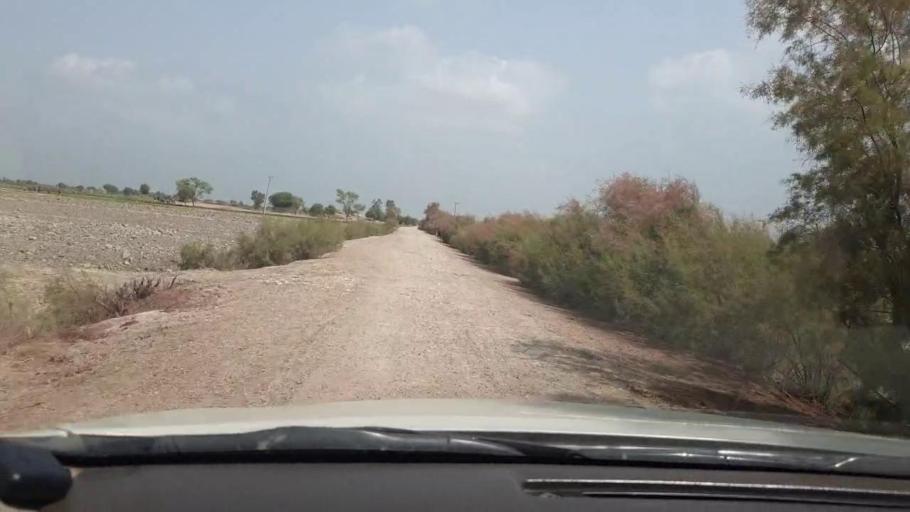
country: PK
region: Sindh
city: Garhi Yasin
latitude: 28.0132
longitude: 68.5286
